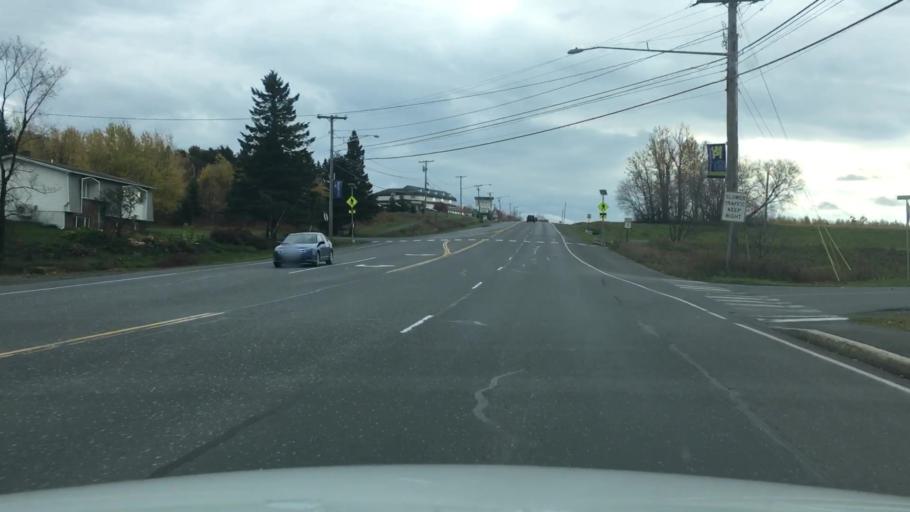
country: US
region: Maine
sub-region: Aroostook County
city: Presque Isle
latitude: 46.6704
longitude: -68.0138
